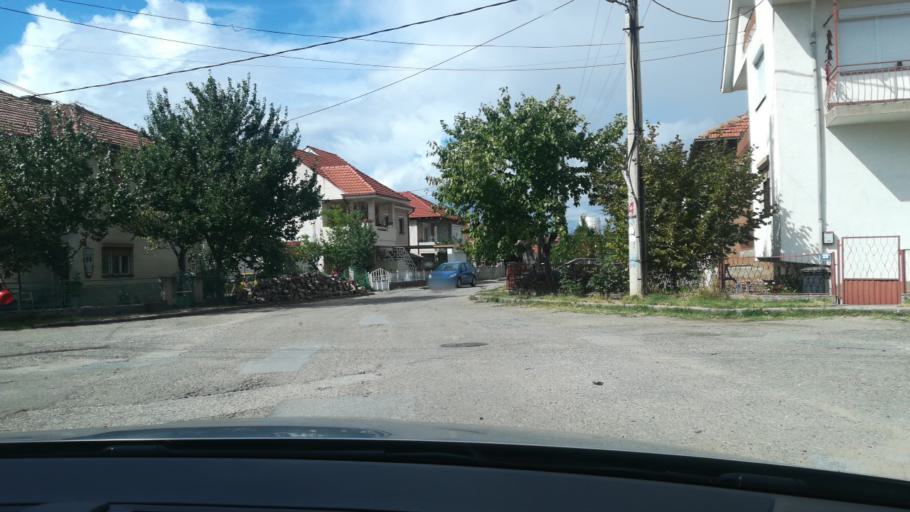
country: MK
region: Delcevo
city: Delcevo
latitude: 41.9639
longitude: 22.7781
